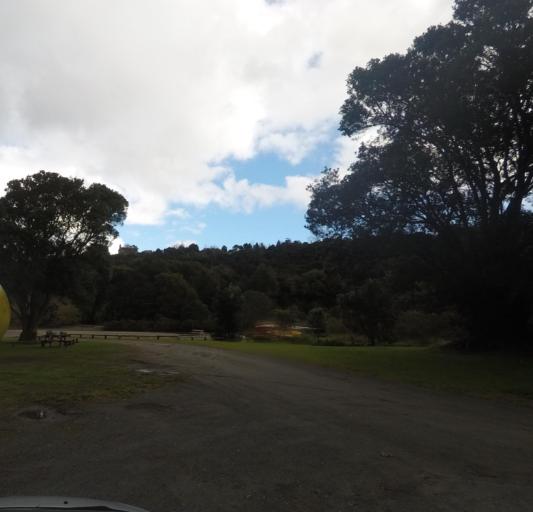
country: NZ
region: Auckland
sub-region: Auckland
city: Warkworth
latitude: -36.3816
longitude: 174.7555
